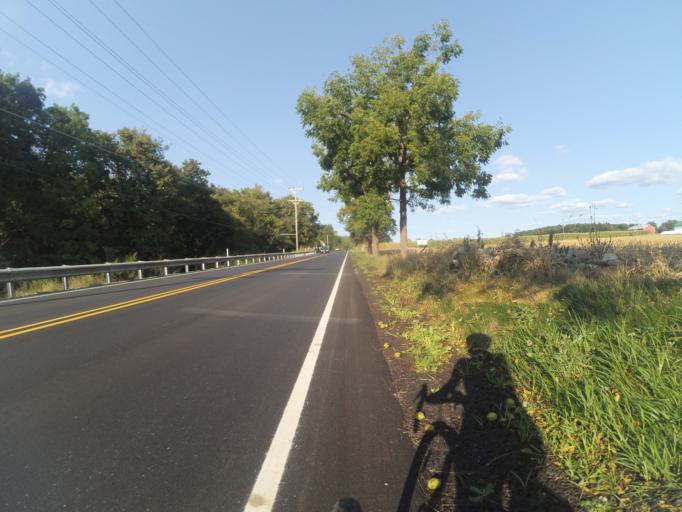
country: US
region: Pennsylvania
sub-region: Centre County
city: Centre Hall
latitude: 40.8013
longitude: -77.7228
